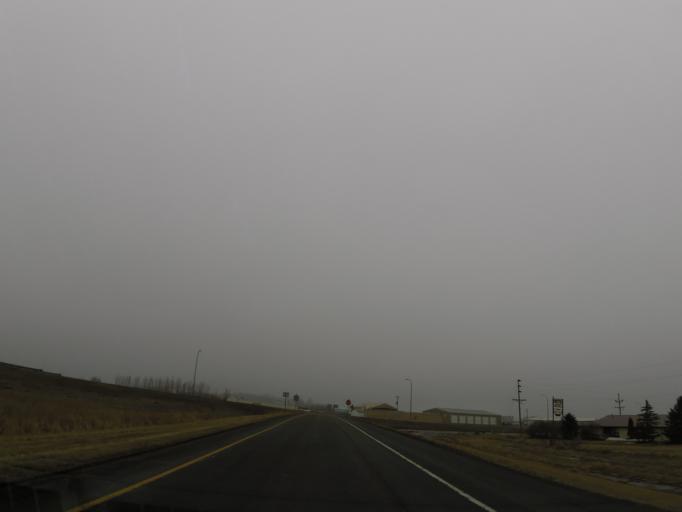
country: US
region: North Dakota
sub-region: Walsh County
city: Grafton
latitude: 48.5701
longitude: -97.1858
